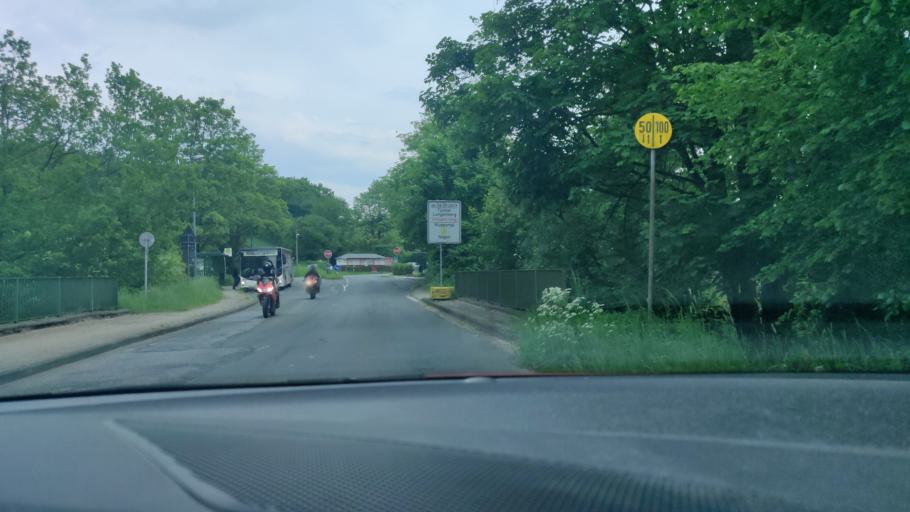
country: DE
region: North Rhine-Westphalia
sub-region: Regierungsbezirk Dusseldorf
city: Velbert
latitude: 51.3376
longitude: 7.0953
